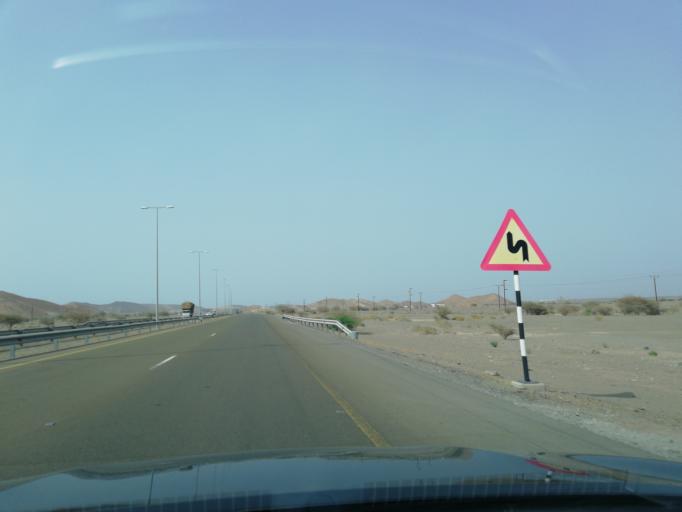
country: OM
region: Al Batinah
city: Al Liwa'
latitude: 24.3583
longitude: 56.5273
